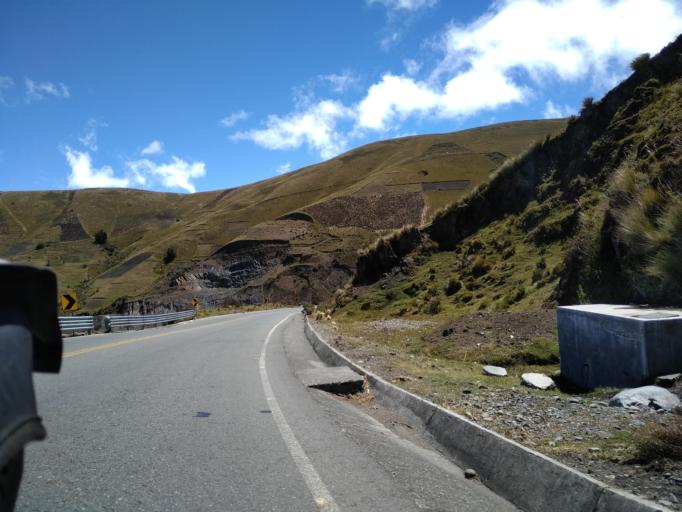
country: EC
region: Cotopaxi
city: Pujili
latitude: -0.9879
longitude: -78.9470
